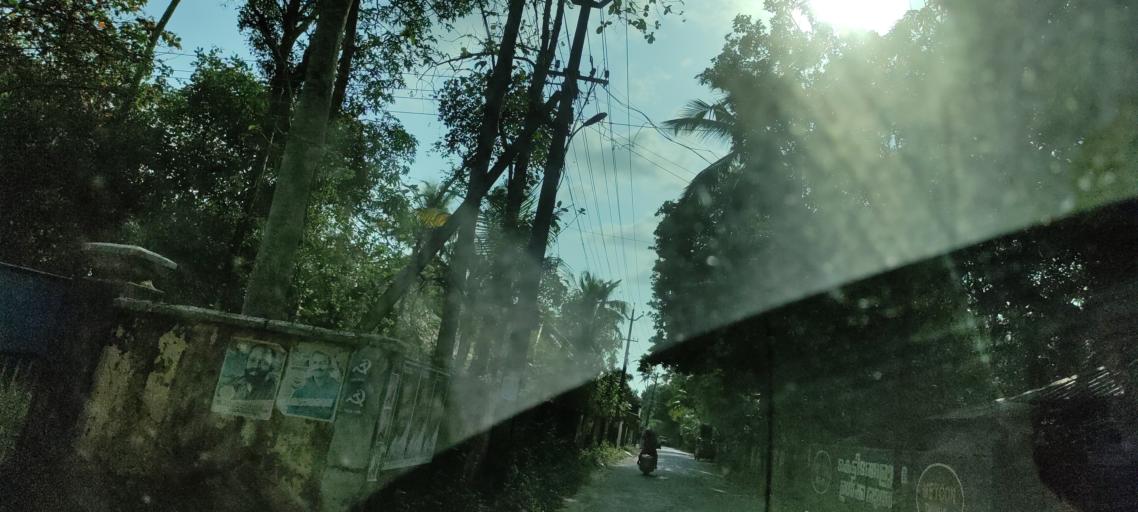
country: IN
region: Kerala
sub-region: Alappuzha
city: Vayalar
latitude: 9.6867
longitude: 76.3084
